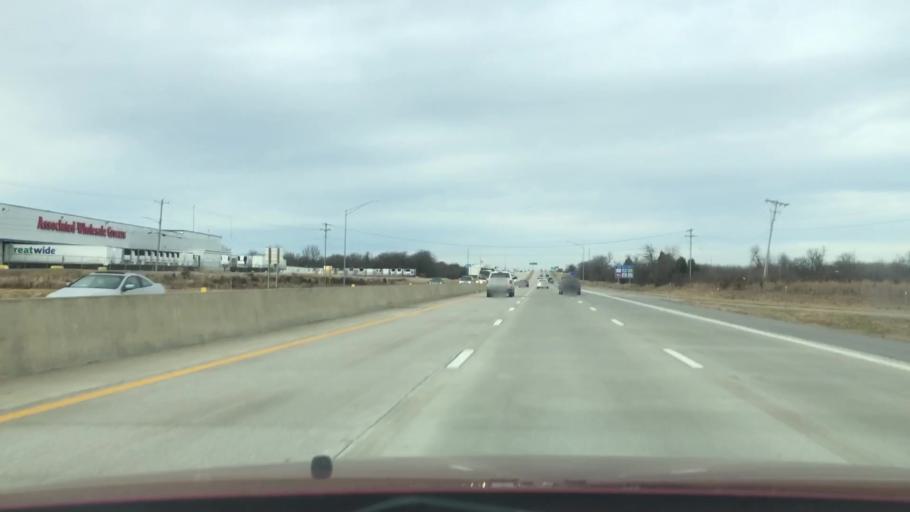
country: US
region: Missouri
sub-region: Greene County
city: Springfield
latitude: 37.2259
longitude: -93.2252
